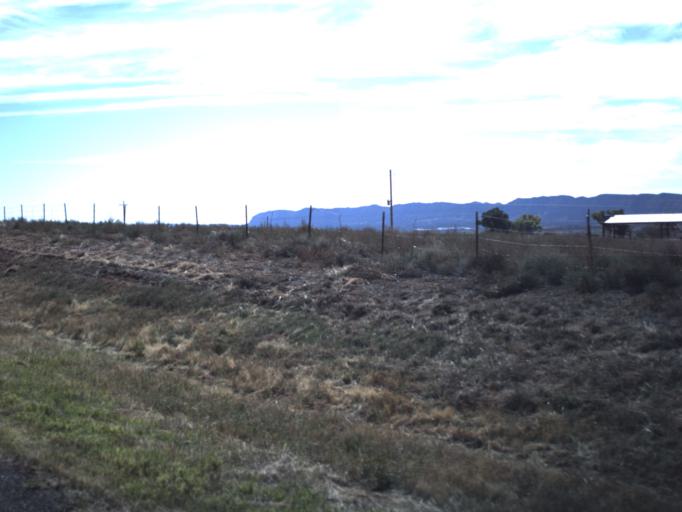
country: US
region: Utah
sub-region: Wayne County
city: Loa
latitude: 37.7630
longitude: -111.5817
